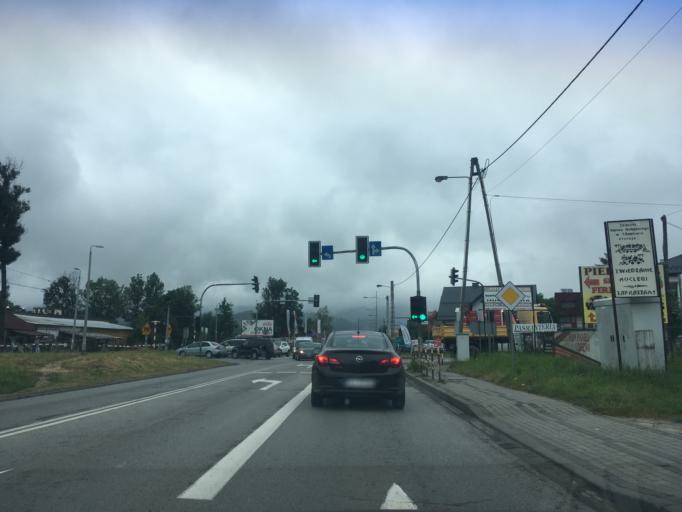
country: PL
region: Lesser Poland Voivodeship
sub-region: Powiat nowotarski
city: Rabka-Zdroj
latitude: 49.6054
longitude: 19.9502
